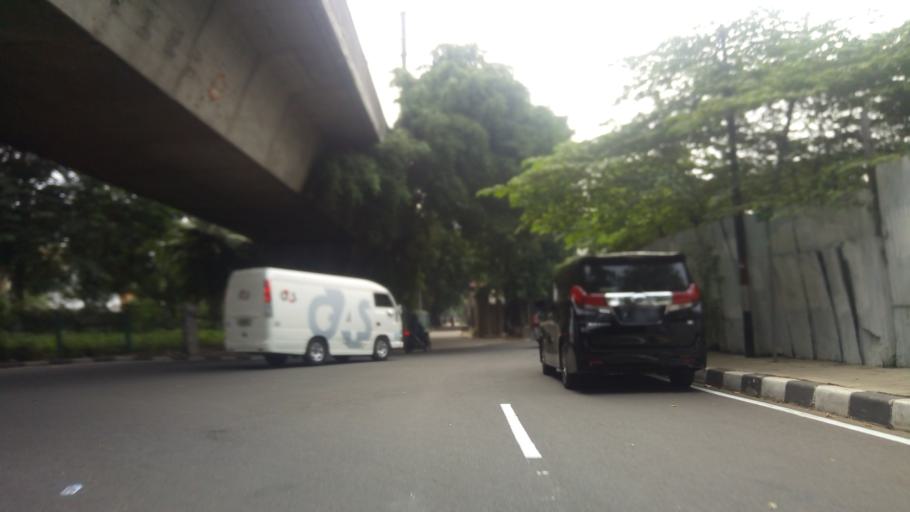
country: ID
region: Jakarta Raya
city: Jakarta
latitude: -6.1924
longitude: 106.8368
